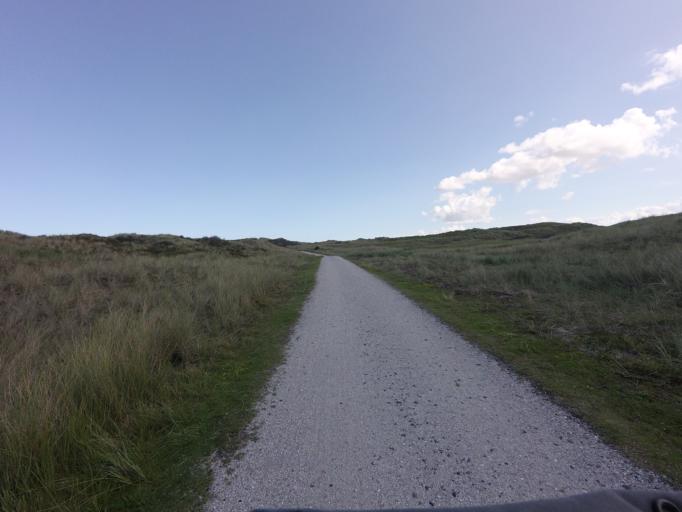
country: NL
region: Friesland
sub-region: Gemeente Terschelling
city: West-Terschelling
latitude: 53.4068
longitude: 5.3003
